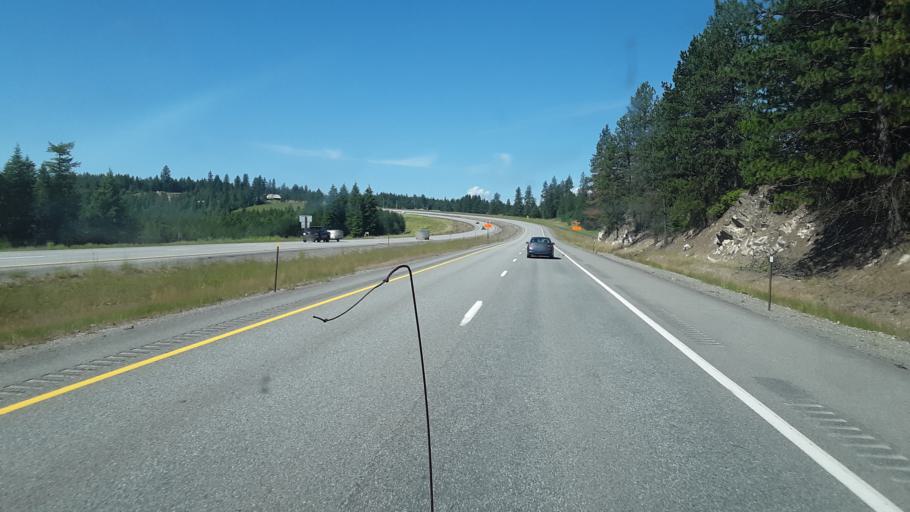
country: US
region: Idaho
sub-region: Kootenai County
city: Spirit Lake
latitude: 47.9909
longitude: -116.6870
